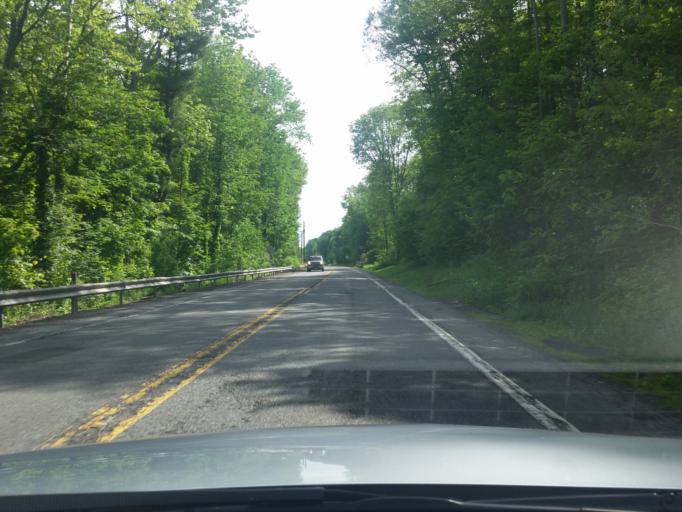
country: US
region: Pennsylvania
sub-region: Luzerne County
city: Back Mountain
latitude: 41.3092
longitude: -76.0349
